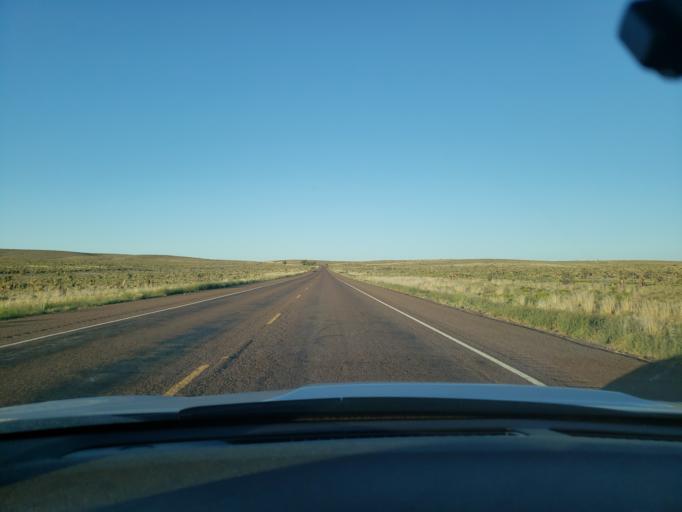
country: US
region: Texas
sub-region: El Paso County
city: Homestead Meadows South
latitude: 31.8342
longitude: -105.8549
